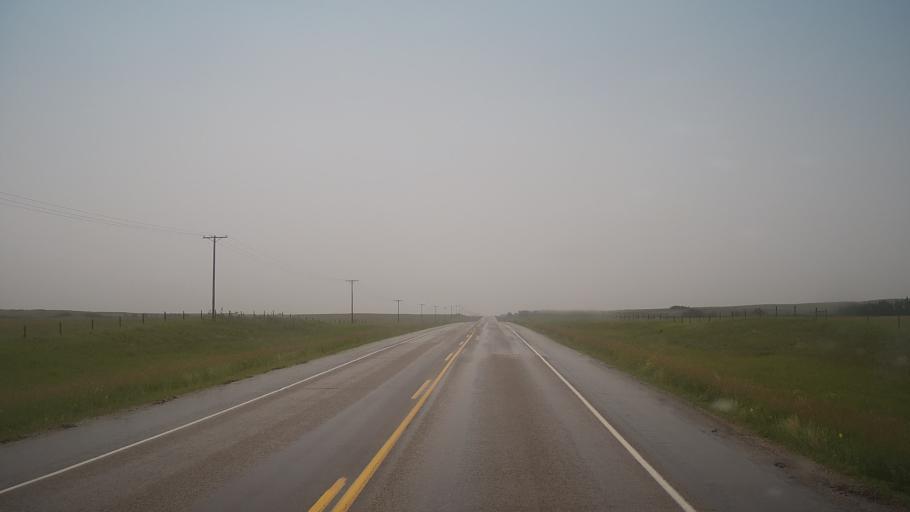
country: CA
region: Saskatchewan
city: Biggar
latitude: 52.0796
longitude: -108.0298
